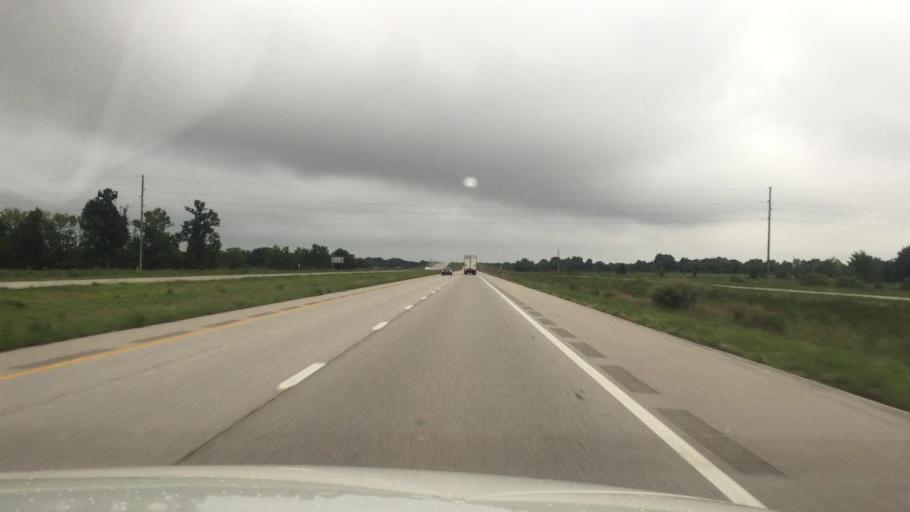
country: US
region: Kansas
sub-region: Montgomery County
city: Coffeyville
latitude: 37.0968
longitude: -95.5897
